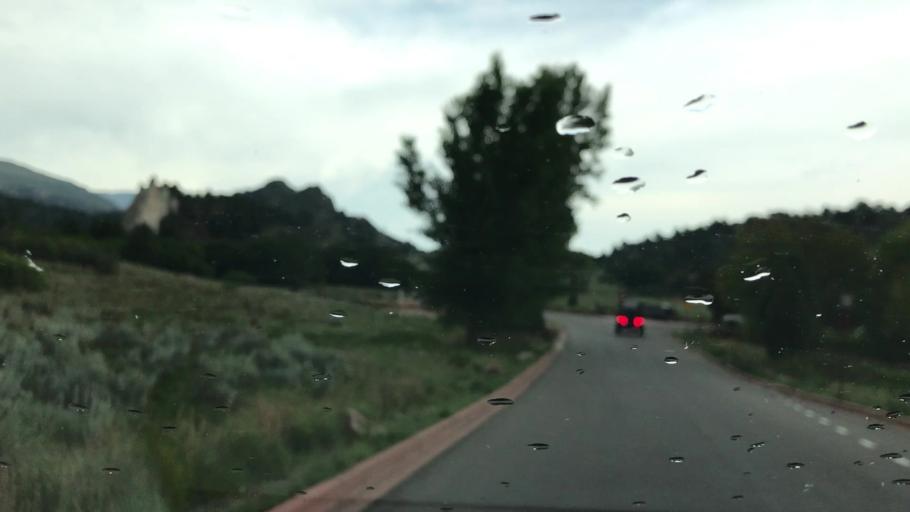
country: US
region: Colorado
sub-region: El Paso County
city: Manitou Springs
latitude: 38.8763
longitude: -104.8782
